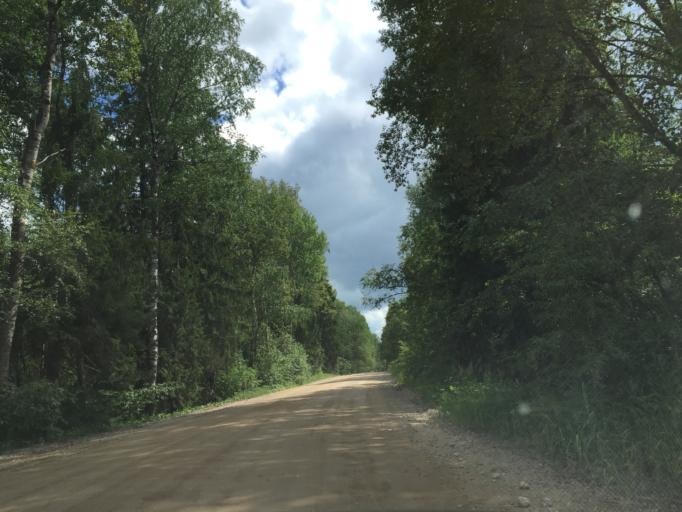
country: LV
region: Ropazu
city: Ropazi
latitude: 56.9177
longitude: 24.7425
